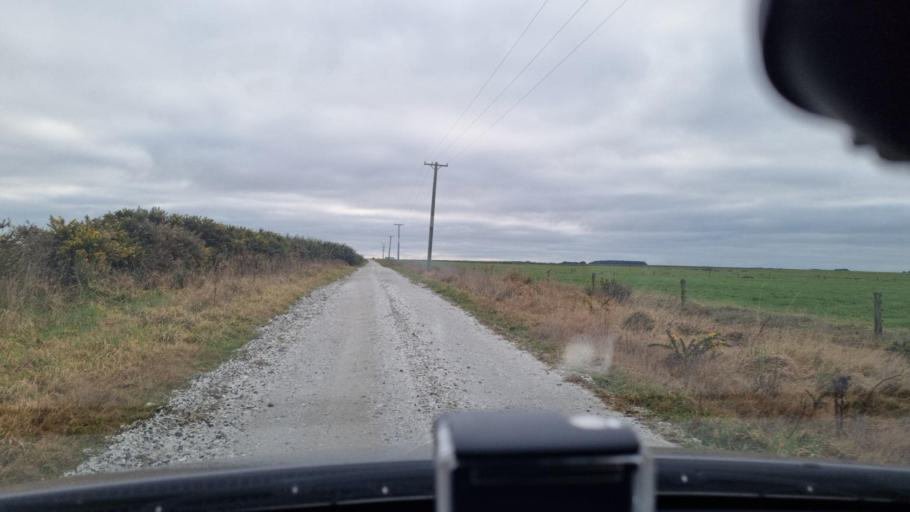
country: NZ
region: Southland
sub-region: Invercargill City
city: Bluff
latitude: -46.5327
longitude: 168.3853
